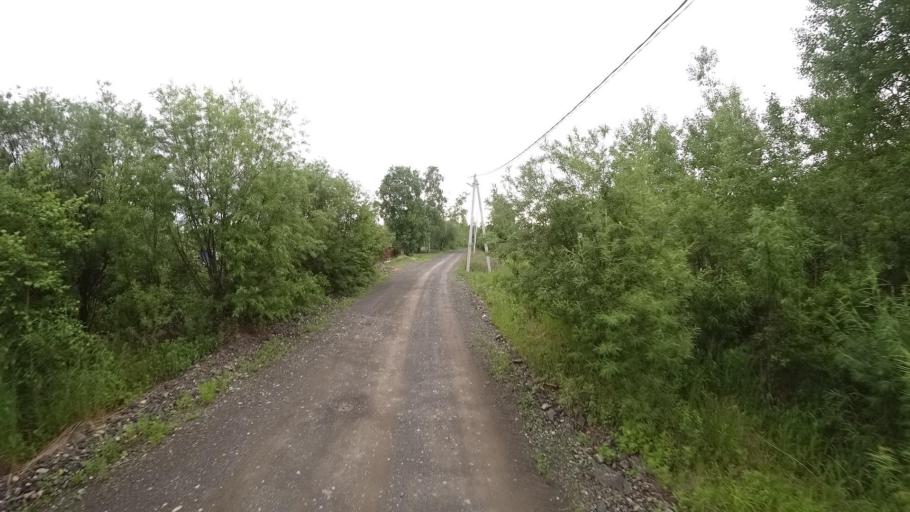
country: RU
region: Khabarovsk Krai
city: Amursk
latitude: 49.9092
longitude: 136.1502
